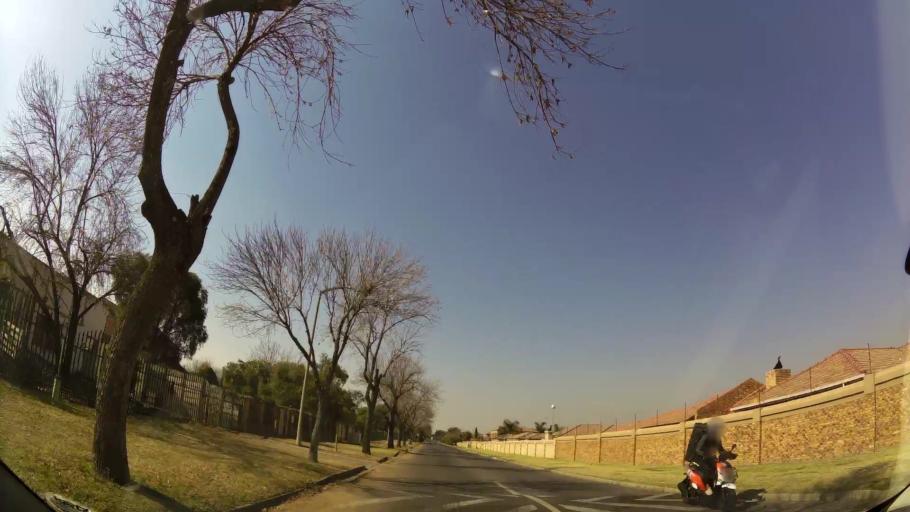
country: ZA
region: Gauteng
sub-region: Ekurhuleni Metropolitan Municipality
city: Boksburg
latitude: -26.1663
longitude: 28.2685
